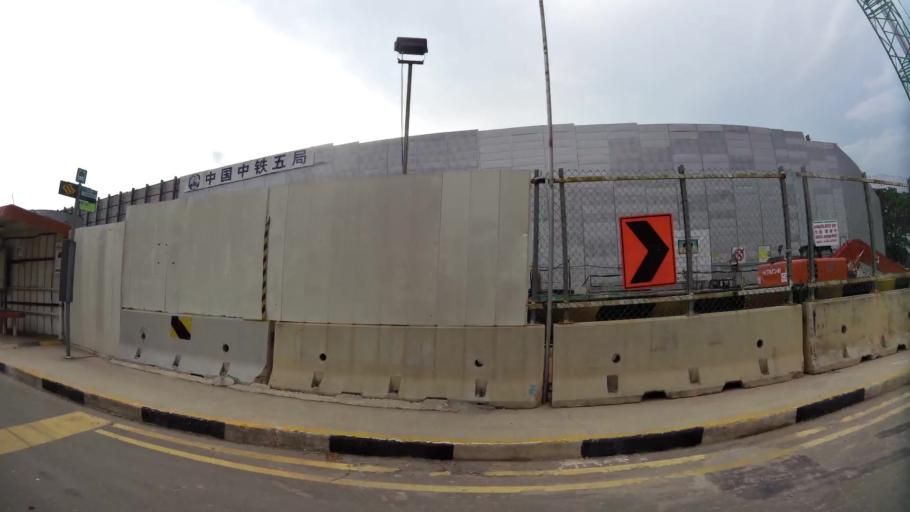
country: SG
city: Singapore
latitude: 1.3847
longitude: 103.8366
